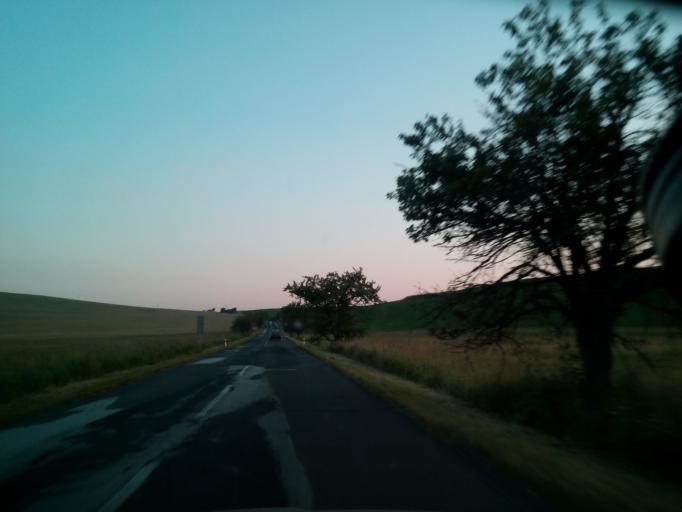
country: SK
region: Presovsky
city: Lubica
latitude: 49.1004
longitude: 20.4377
